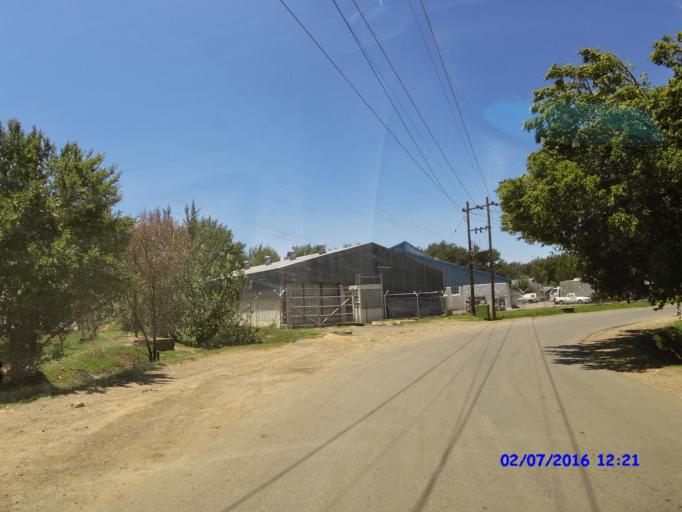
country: LS
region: Maseru
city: Maseru
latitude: -29.2948
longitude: 27.4808
